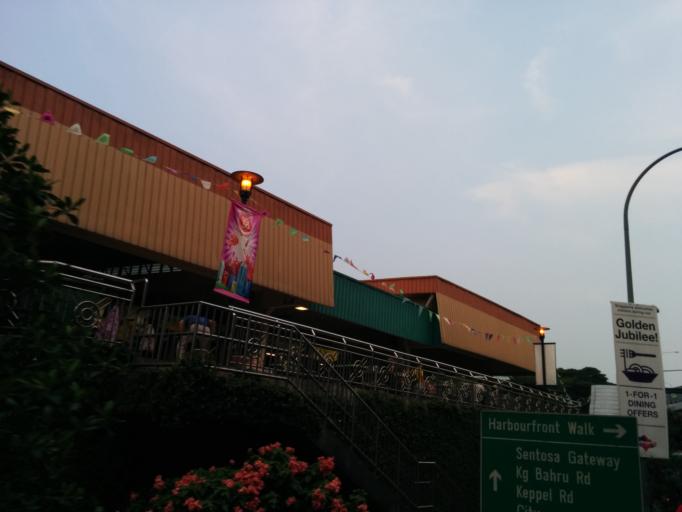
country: SG
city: Singapore
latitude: 1.2663
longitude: 103.8194
